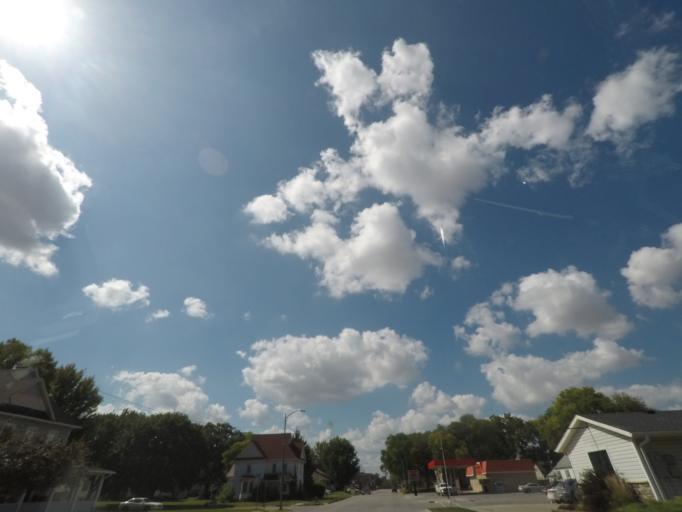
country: US
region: Iowa
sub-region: Story County
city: Nevada
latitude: 42.0227
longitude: -93.4489
